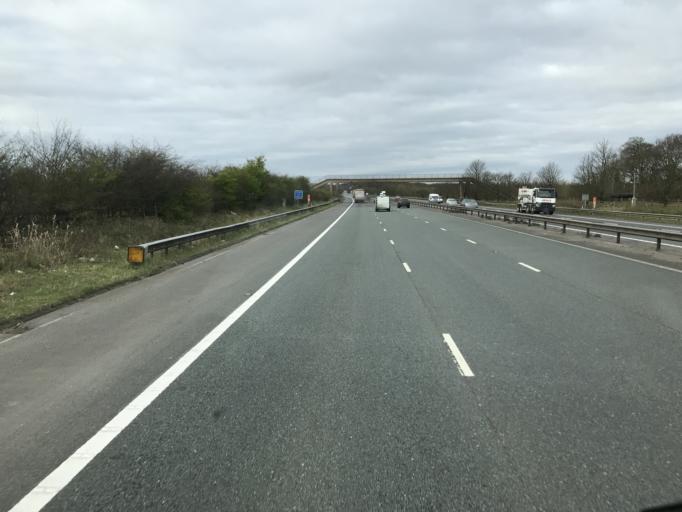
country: GB
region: England
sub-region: Warrington
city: Burtonwood
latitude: 53.4125
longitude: -2.6876
